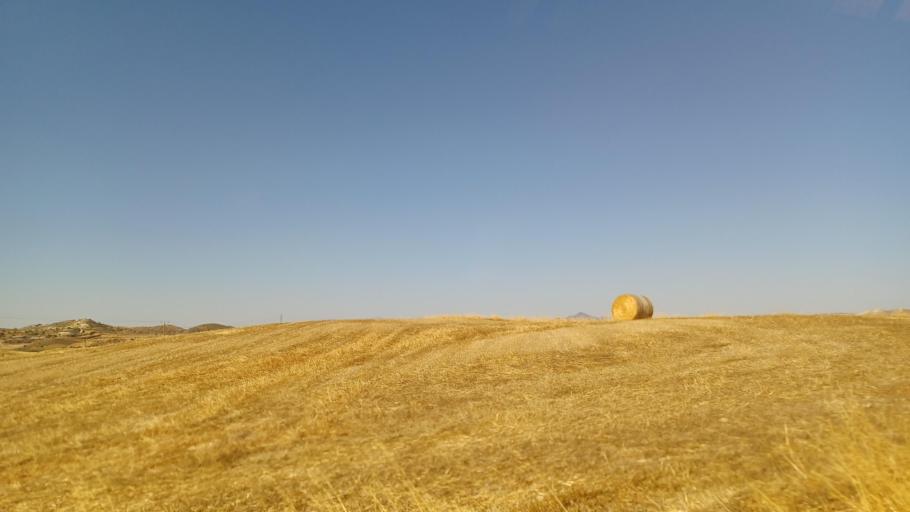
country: CY
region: Larnaka
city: Troulloi
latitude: 35.0112
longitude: 33.6036
